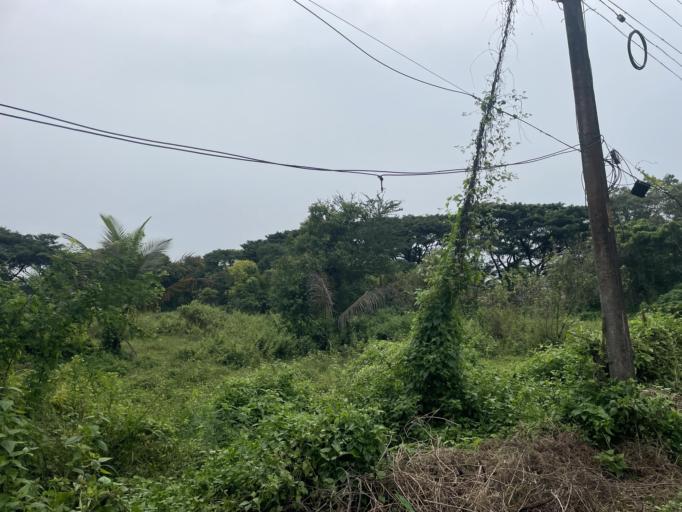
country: IN
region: Kerala
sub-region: Palakkad district
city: Chittur
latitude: 10.6934
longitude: 76.7417
